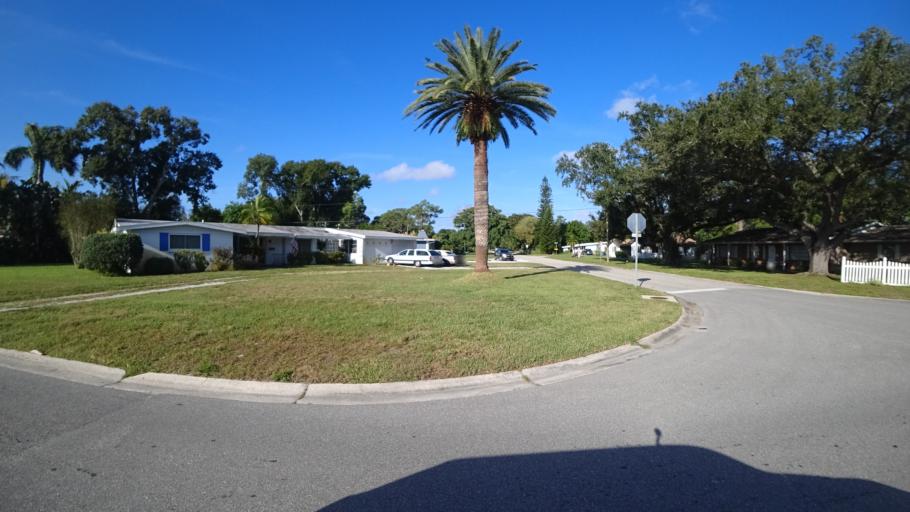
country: US
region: Florida
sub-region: Manatee County
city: West Bradenton
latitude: 27.4865
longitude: -82.5998
